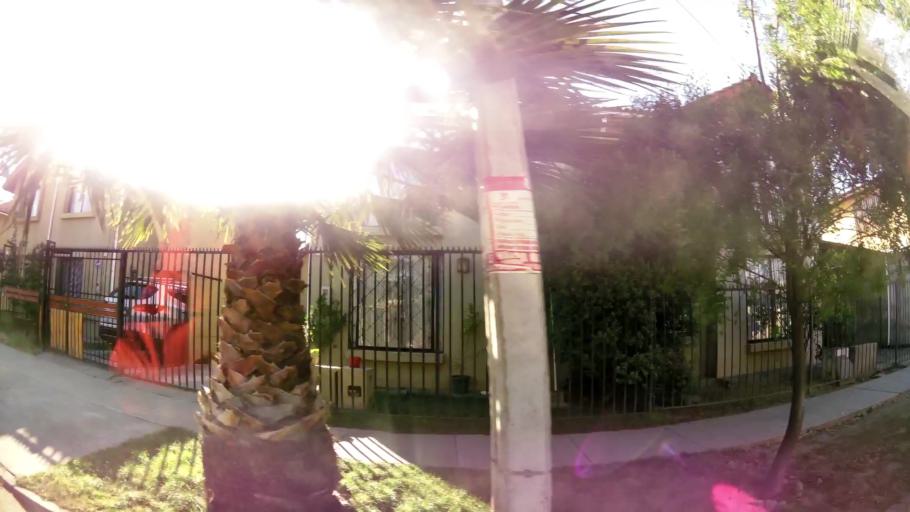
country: CL
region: Santiago Metropolitan
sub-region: Provincia de Maipo
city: San Bernardo
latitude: -33.5493
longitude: -70.7618
